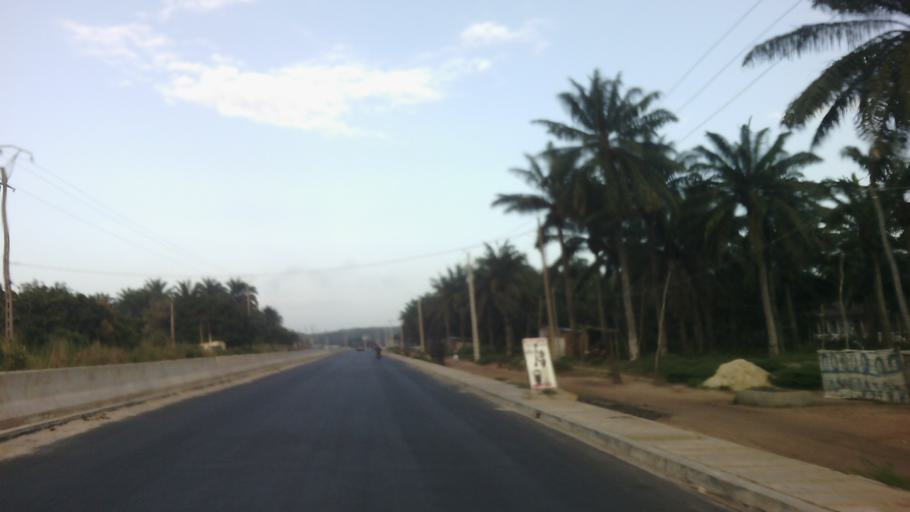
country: BJ
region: Atlantique
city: Hevie
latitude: 6.3824
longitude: 2.1761
